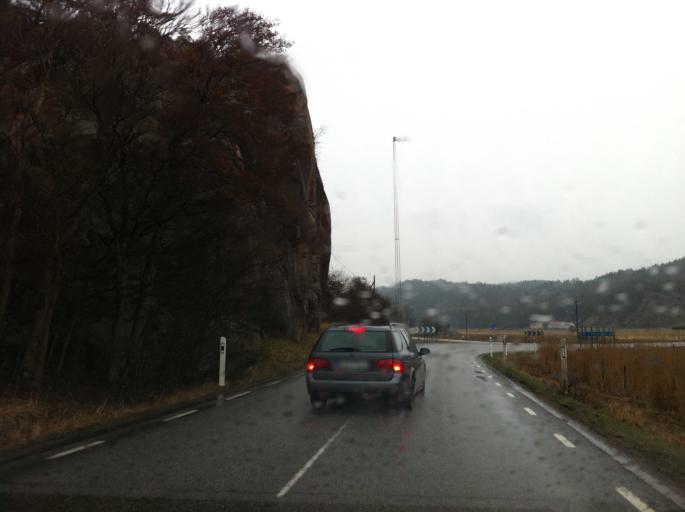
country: SE
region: Vaestra Goetaland
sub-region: Lysekils Kommun
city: Brastad
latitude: 58.4599
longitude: 11.4529
